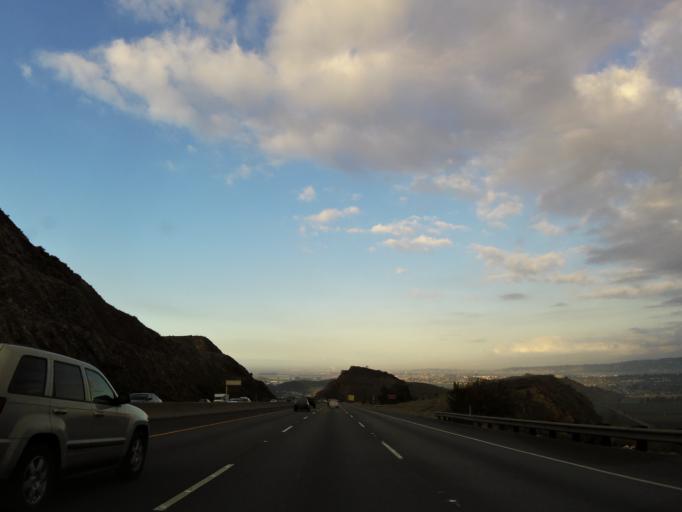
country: US
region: California
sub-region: Ventura County
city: Casa Conejo
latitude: 34.2013
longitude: -118.9684
